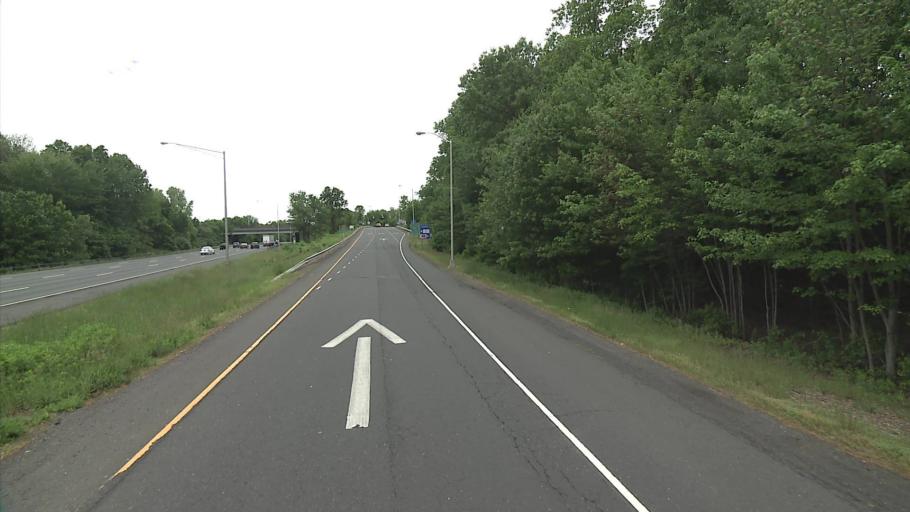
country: US
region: Connecticut
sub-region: Middlesex County
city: Cromwell
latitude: 41.6528
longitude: -72.6727
